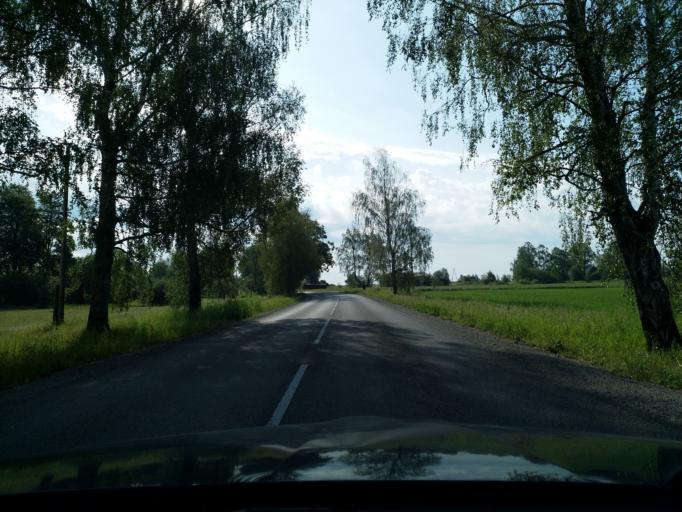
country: LV
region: Talsu Rajons
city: Sabile
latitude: 56.9493
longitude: 22.3643
